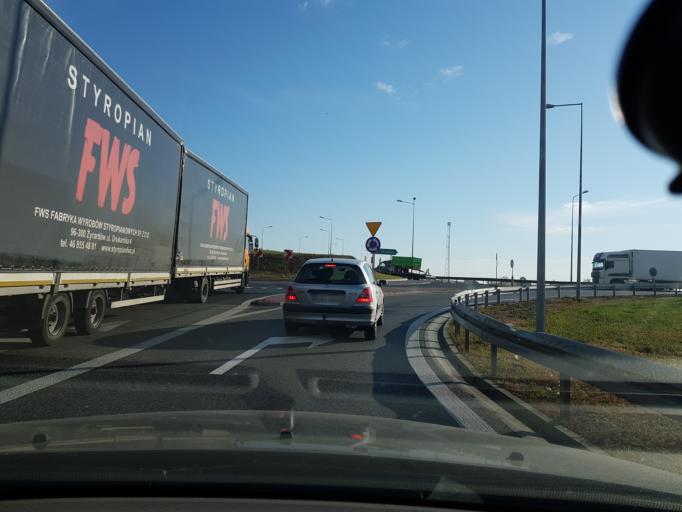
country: PL
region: Masovian Voivodeship
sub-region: Powiat zyrardowski
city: Wiskitki
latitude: 52.0911
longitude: 20.3630
